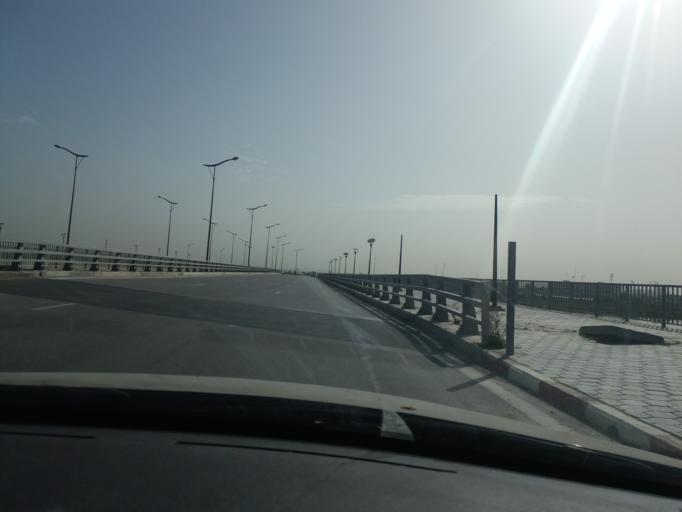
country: TN
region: Tunis
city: Tunis
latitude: 36.8054
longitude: 10.1954
